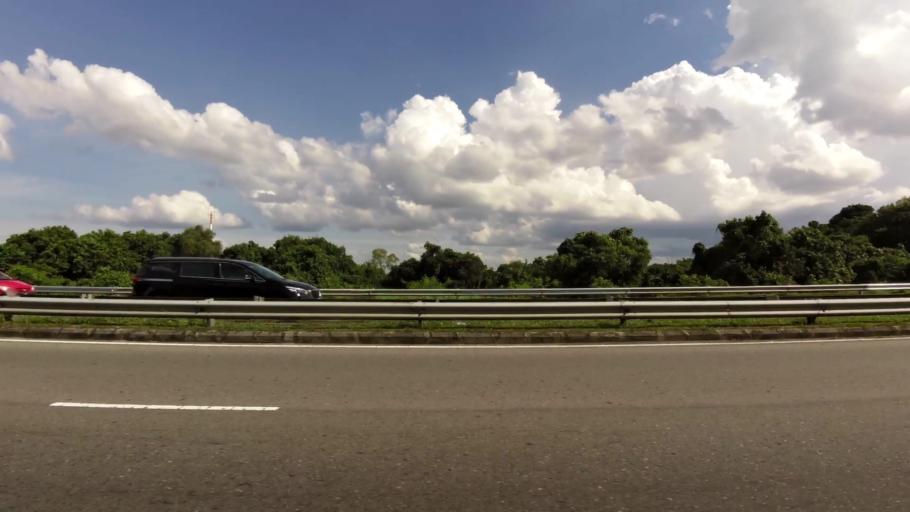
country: BN
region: Brunei and Muara
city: Bandar Seri Begawan
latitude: 4.9512
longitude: 114.9488
